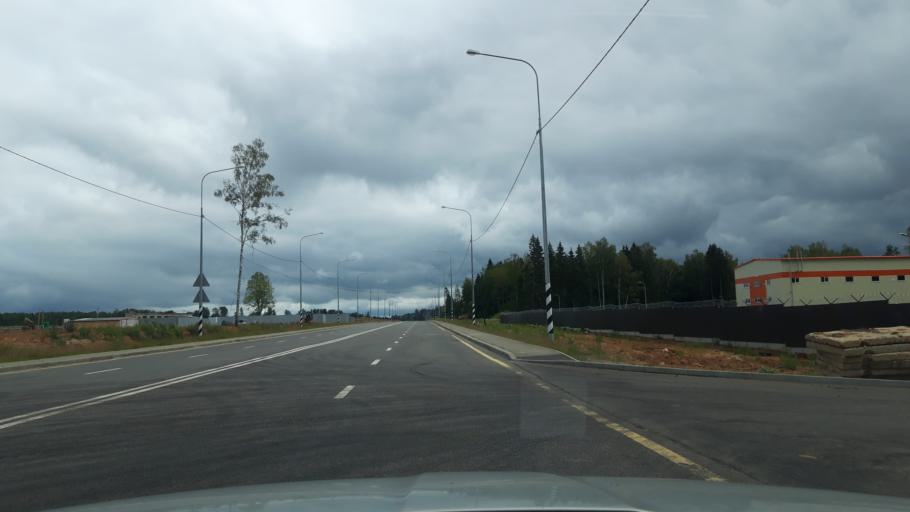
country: RU
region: Moskovskaya
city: Lozhki
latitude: 56.0802
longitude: 37.0933
